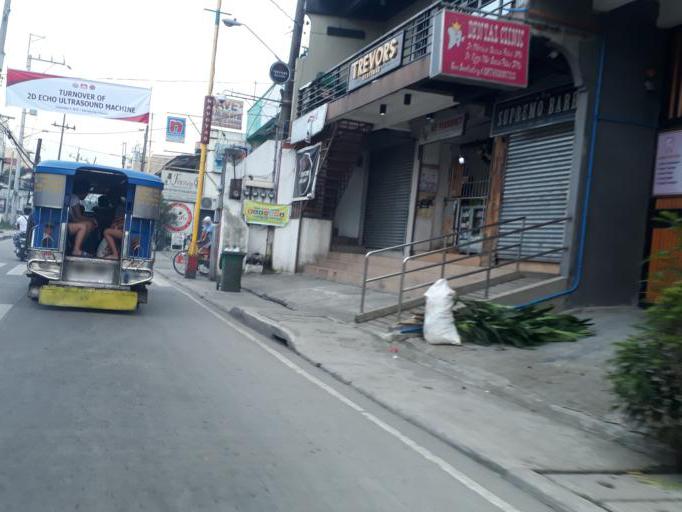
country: PH
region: Calabarzon
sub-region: Province of Rizal
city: Navotas
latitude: 14.6603
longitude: 120.9465
